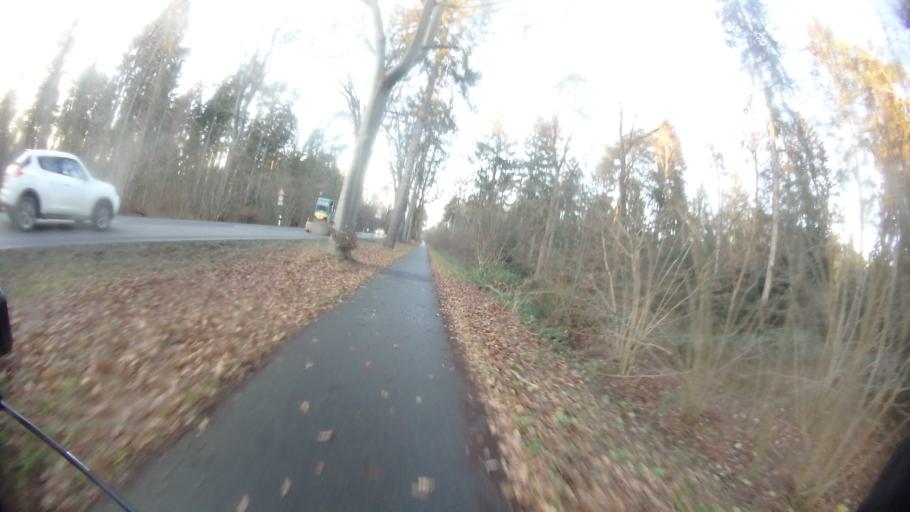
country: DE
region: Schleswig-Holstein
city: Ratekau
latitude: 53.9941
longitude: 10.7081
